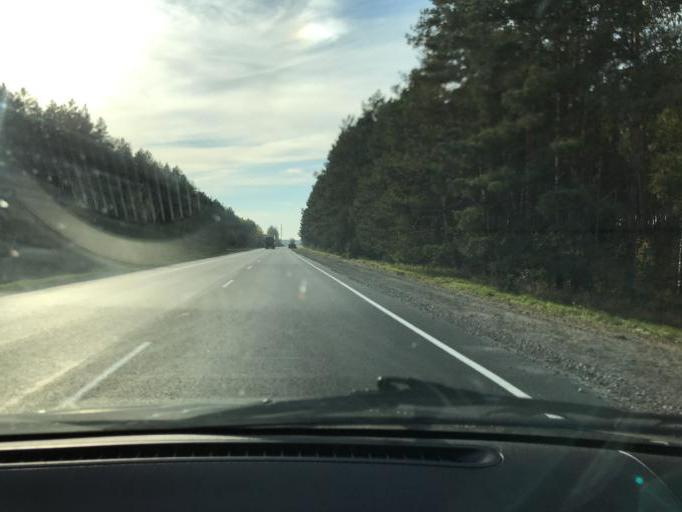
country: BY
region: Brest
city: Horad Pinsk
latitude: 52.1705
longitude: 26.0316
